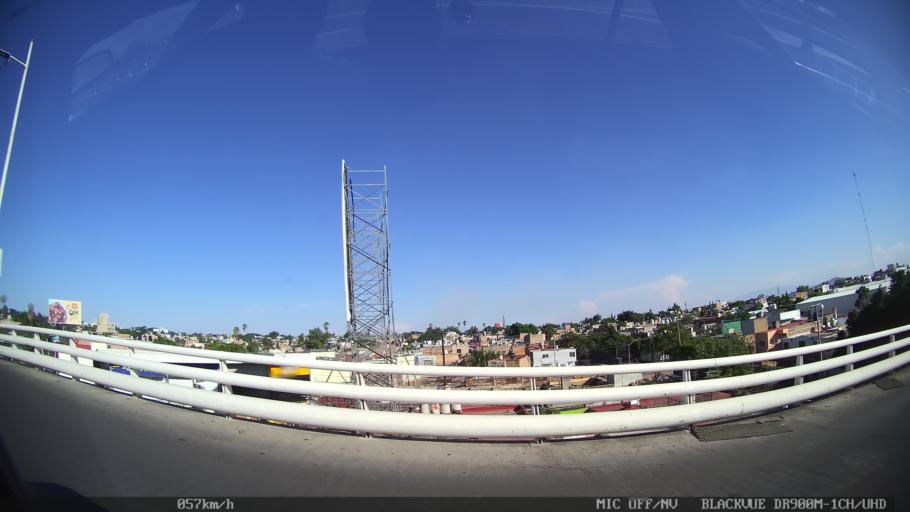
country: MX
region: Jalisco
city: Tlaquepaque
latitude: 20.6910
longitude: -103.3129
